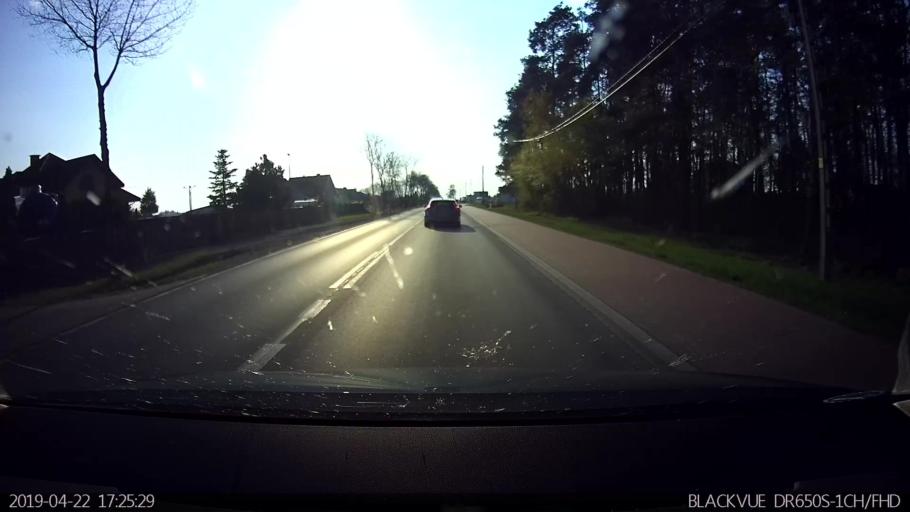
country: PL
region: Masovian Voivodeship
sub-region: Powiat sokolowski
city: Sokolow Podlaski
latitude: 52.3941
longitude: 22.2896
